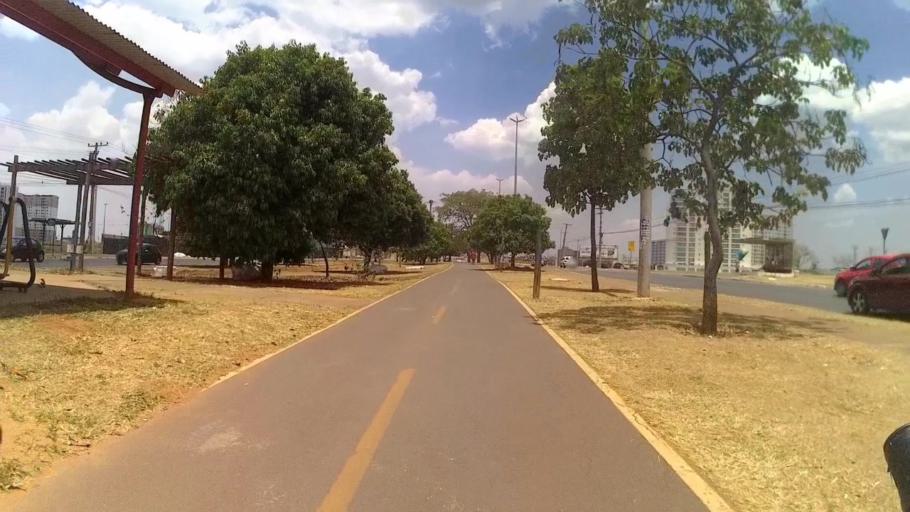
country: BR
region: Federal District
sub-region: Brasilia
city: Brasilia
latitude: -15.8763
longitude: -48.0816
